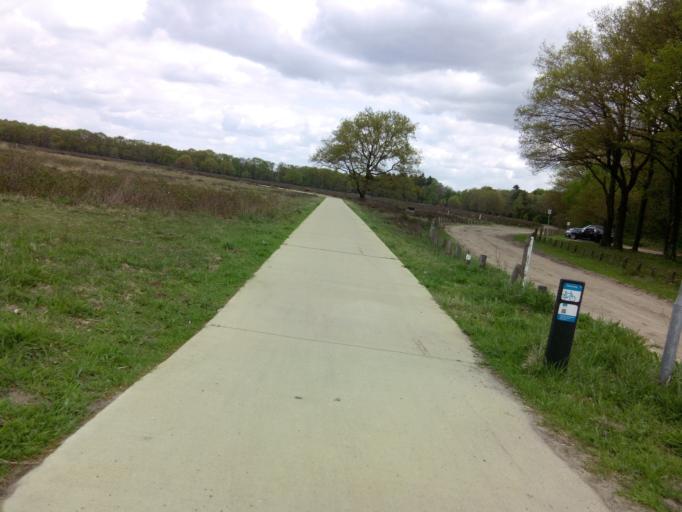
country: NL
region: Gelderland
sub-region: Gemeente Renkum
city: Renkum
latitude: 52.0380
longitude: 5.7270
